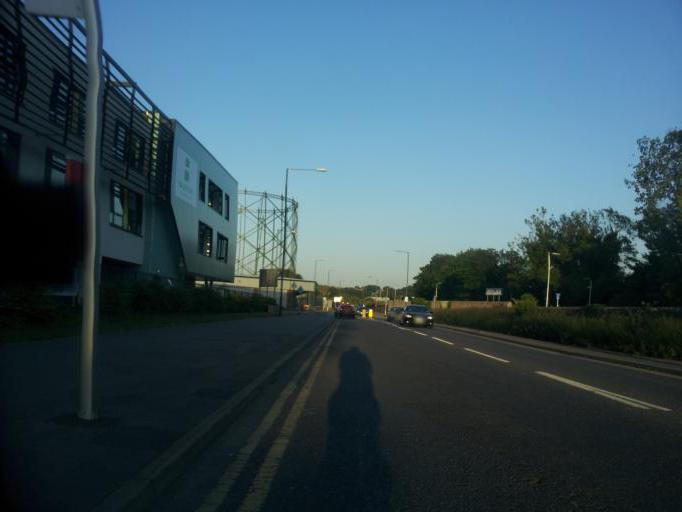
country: GB
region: England
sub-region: Kent
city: Dartford
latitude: 51.4497
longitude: 0.2143
